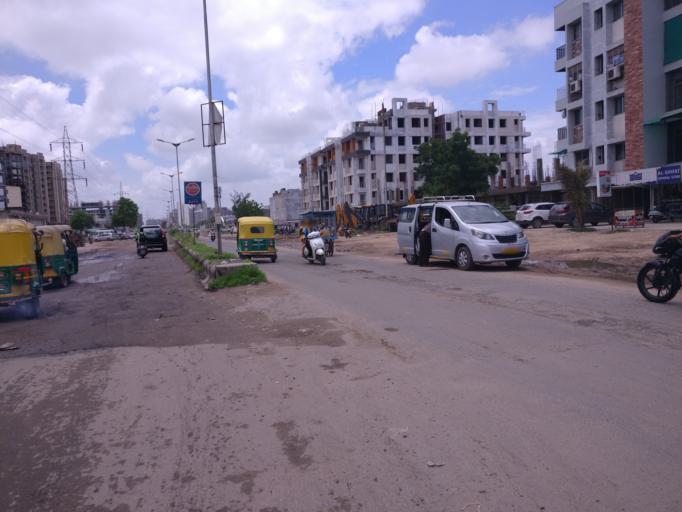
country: IN
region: Gujarat
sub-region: Ahmadabad
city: Sarkhej
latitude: 22.9906
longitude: 72.5149
